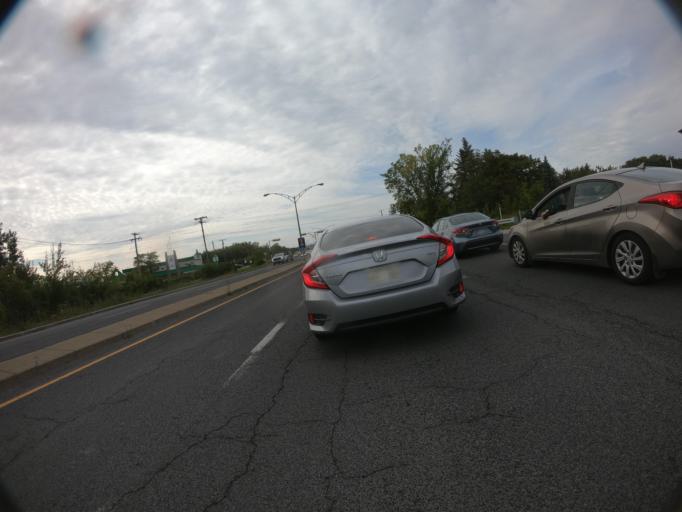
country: CA
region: Quebec
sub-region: Monteregie
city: Chambly
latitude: 45.4416
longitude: -73.2704
